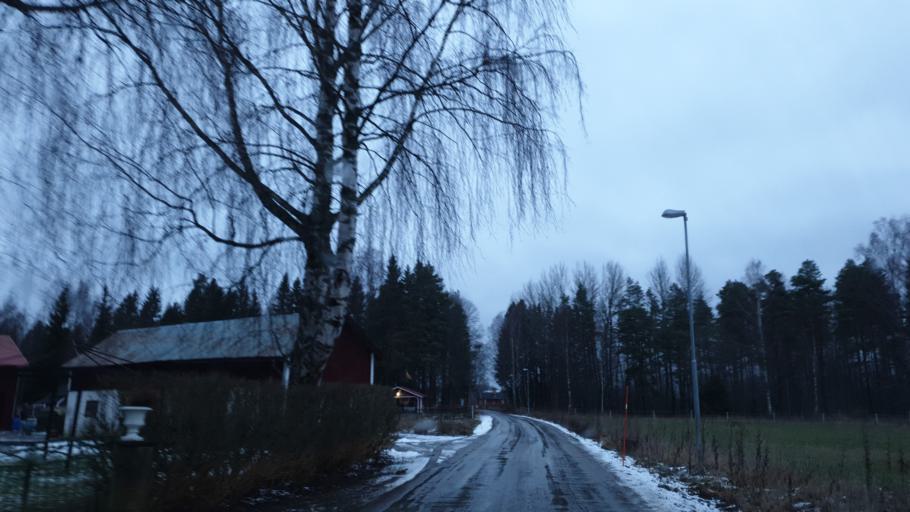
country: SE
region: Uppsala
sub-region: Tierps Kommun
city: Tierp
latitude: 60.3398
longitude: 17.4751
